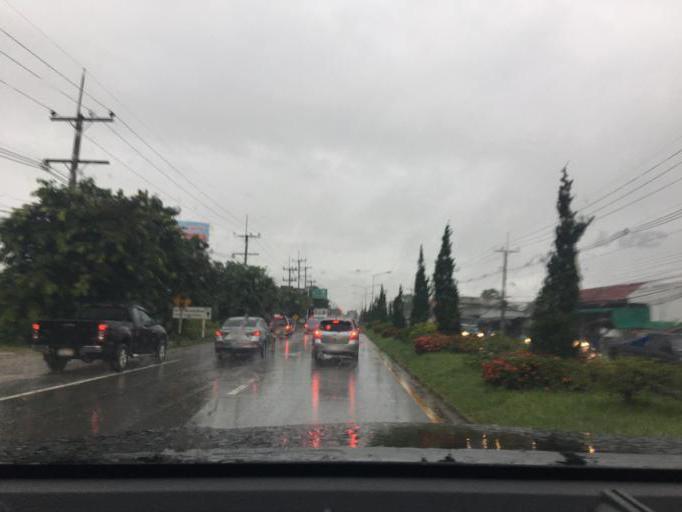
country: TH
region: Chiang Rai
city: Chiang Rai
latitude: 20.0069
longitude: 99.8678
